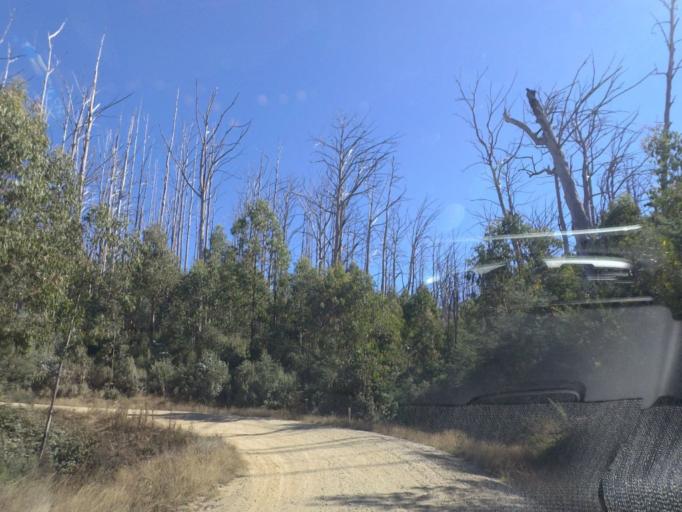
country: AU
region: Victoria
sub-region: Murrindindi
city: Alexandra
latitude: -37.4001
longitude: 145.8101
